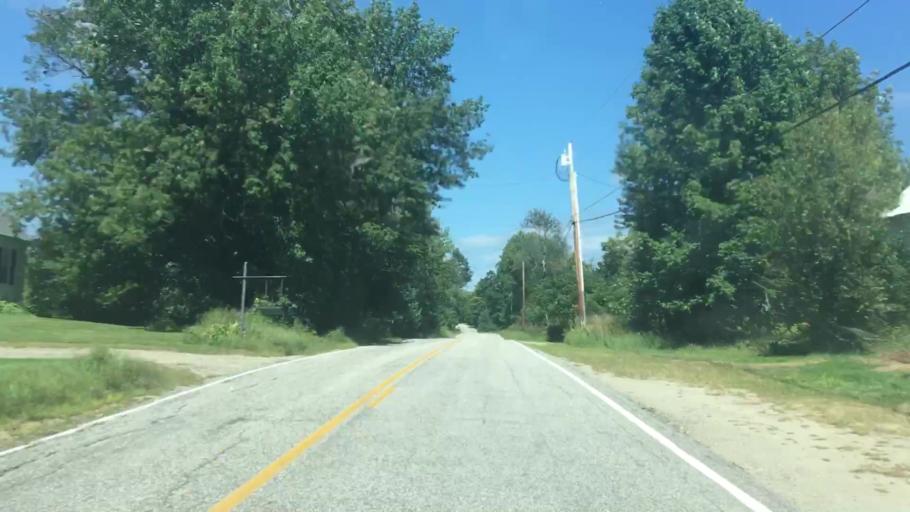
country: US
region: Maine
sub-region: Kennebec County
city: Monmouth
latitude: 44.1825
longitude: -69.9395
